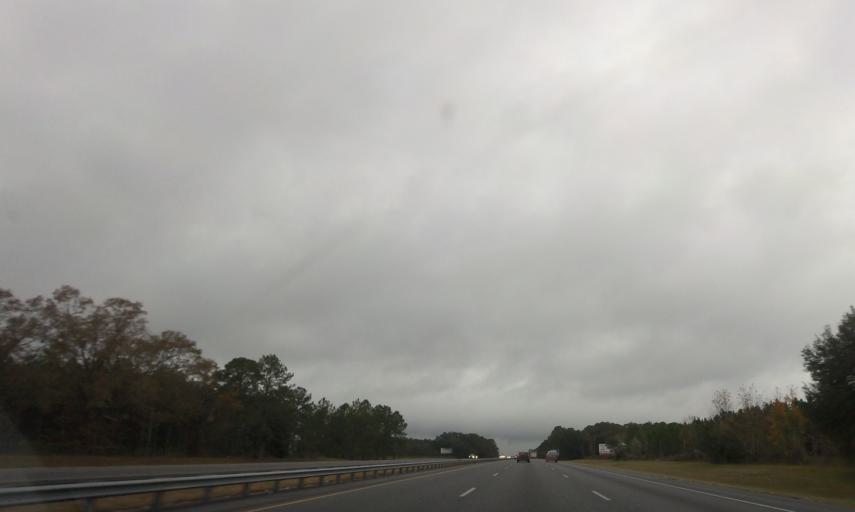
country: US
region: Georgia
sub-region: Lowndes County
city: Valdosta
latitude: 30.7312
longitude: -83.2621
